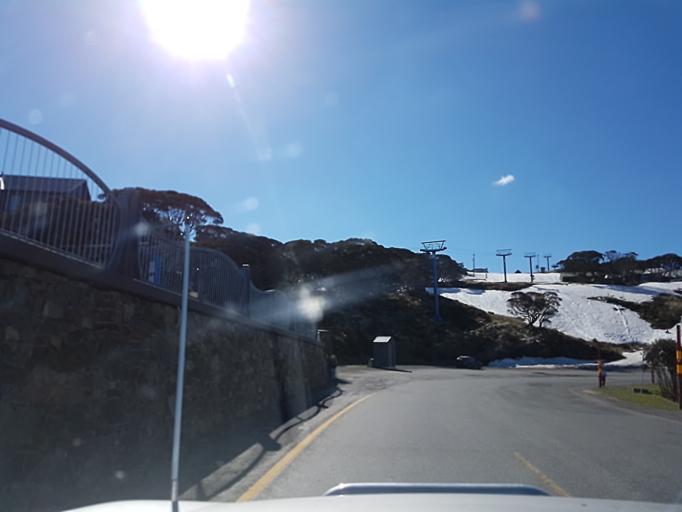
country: AU
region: Victoria
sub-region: Alpine
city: Mount Beauty
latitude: -36.9915
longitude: 147.1485
